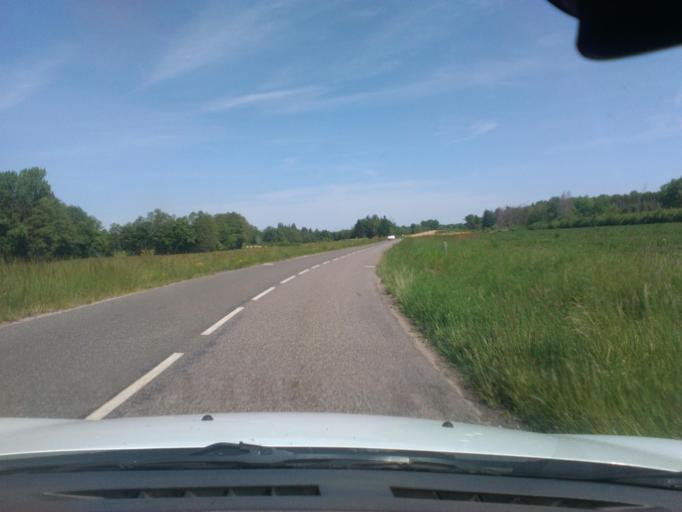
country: FR
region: Lorraine
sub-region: Departement des Vosges
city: Jeanmenil
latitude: 48.3022
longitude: 6.6839
